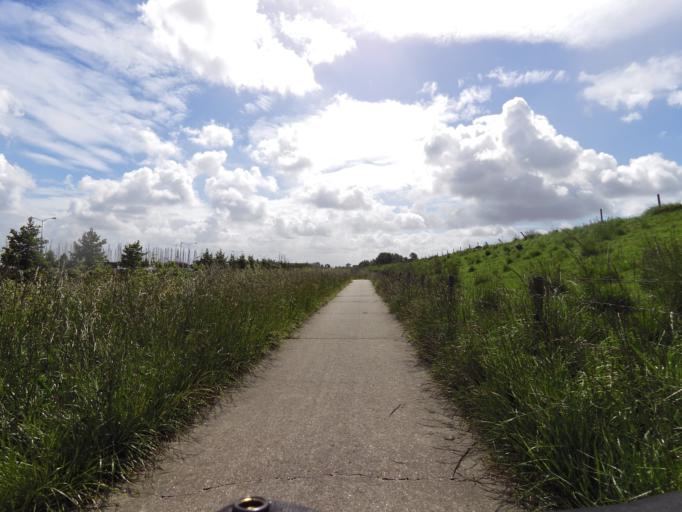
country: NL
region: Zeeland
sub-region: Schouwen-Duiveland
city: Bruinisse
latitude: 51.6720
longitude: 4.0757
